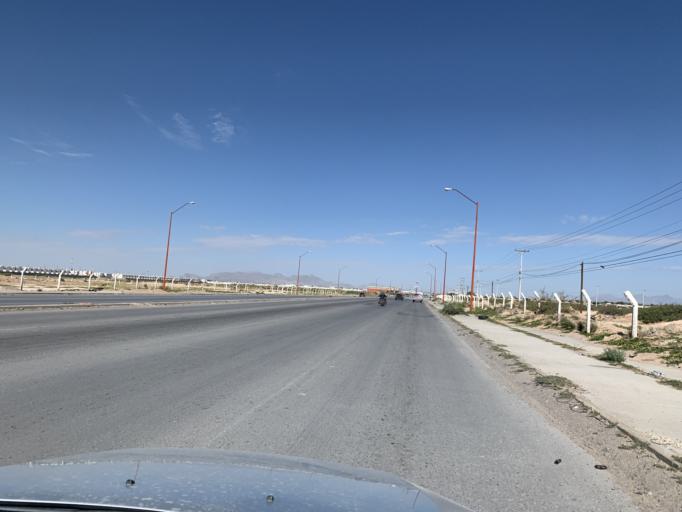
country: US
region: Texas
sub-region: El Paso County
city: San Elizario
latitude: 31.5734
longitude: -106.3522
